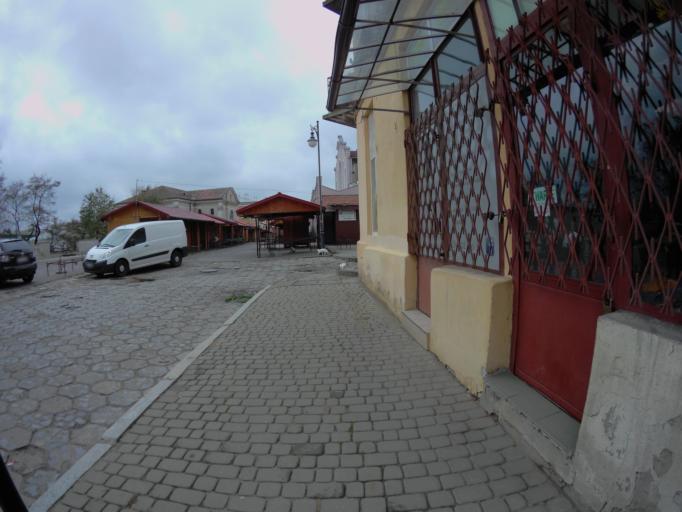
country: PL
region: Subcarpathian Voivodeship
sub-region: Powiat jaroslawski
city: Jaroslaw
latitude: 50.0177
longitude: 22.6845
